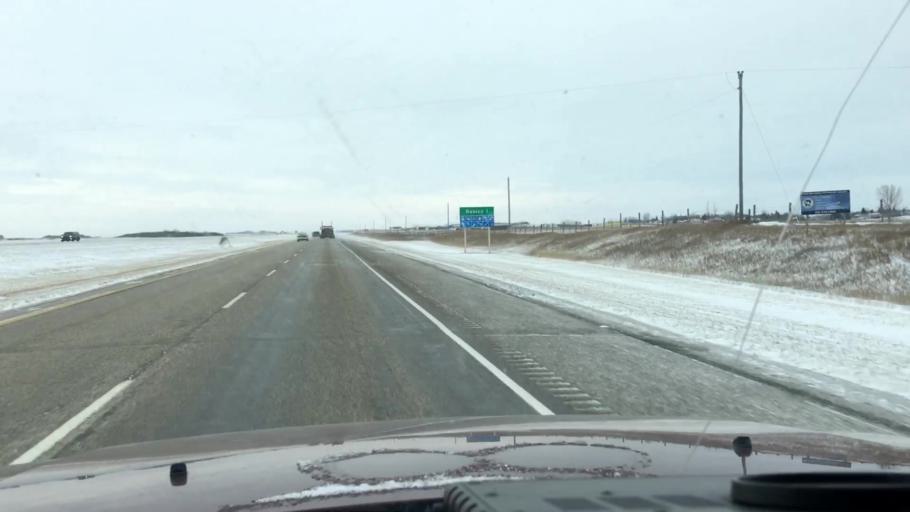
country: CA
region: Saskatchewan
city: Saskatoon
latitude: 51.6419
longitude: -106.4352
